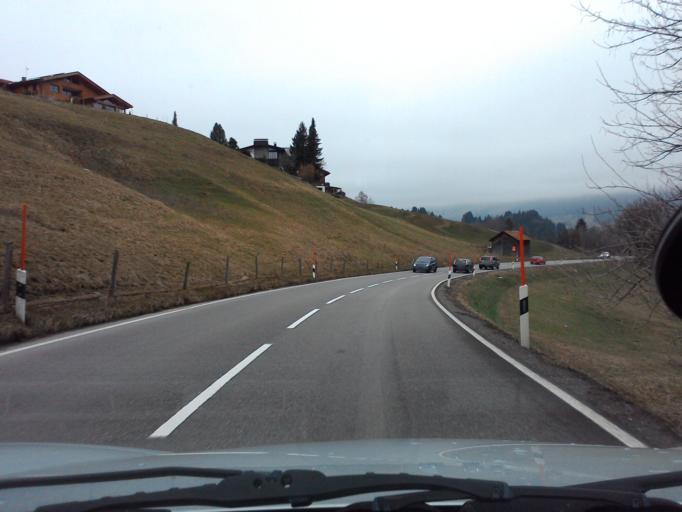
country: DE
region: Bavaria
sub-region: Swabia
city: Oberstdorf
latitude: 47.4105
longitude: 10.2567
